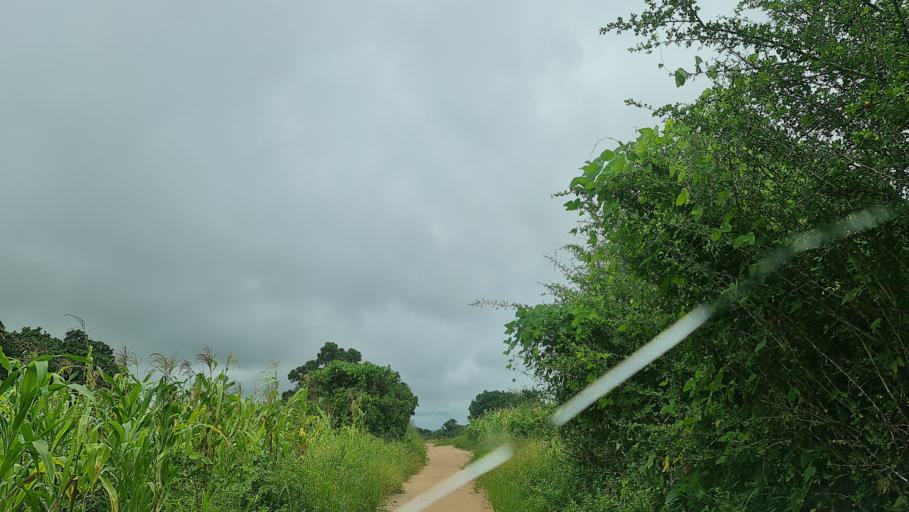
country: MW
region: Southern Region
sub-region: Nsanje District
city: Nsanje
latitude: -17.3374
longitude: 35.7188
